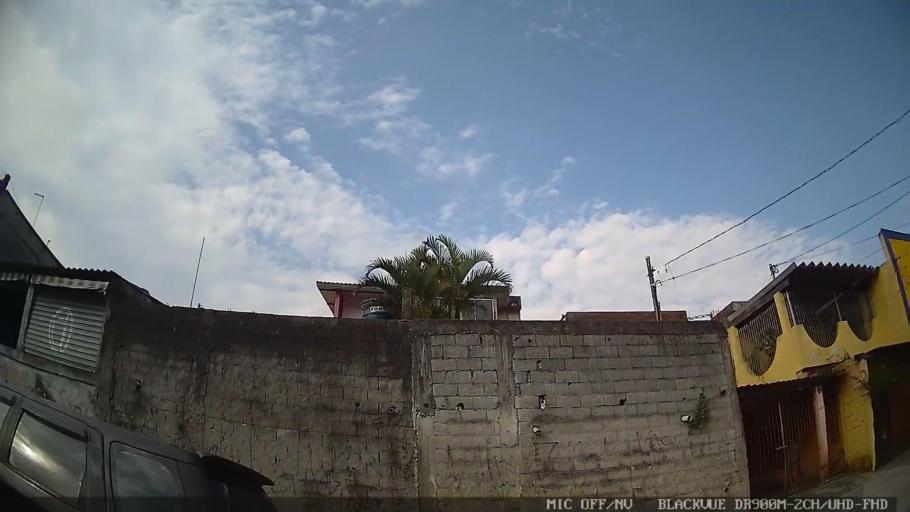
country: BR
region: Sao Paulo
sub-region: Ferraz De Vasconcelos
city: Ferraz de Vasconcelos
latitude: -23.5030
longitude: -46.4050
